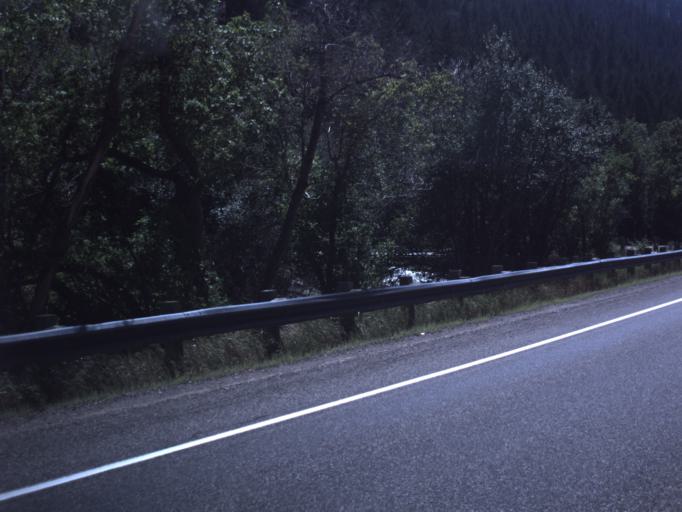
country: US
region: Utah
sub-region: Cache County
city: North Logan
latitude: 41.7796
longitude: -111.6452
